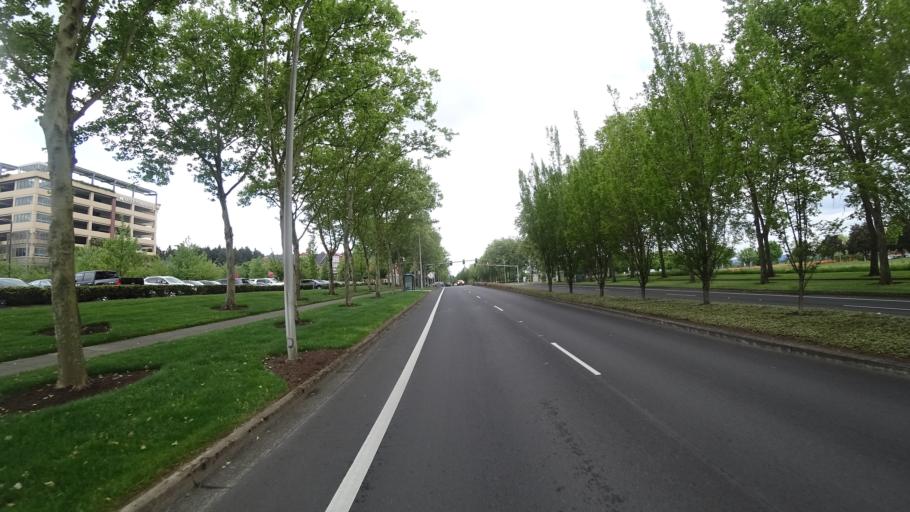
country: US
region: Oregon
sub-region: Washington County
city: Rockcreek
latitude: 45.5411
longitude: -122.8753
